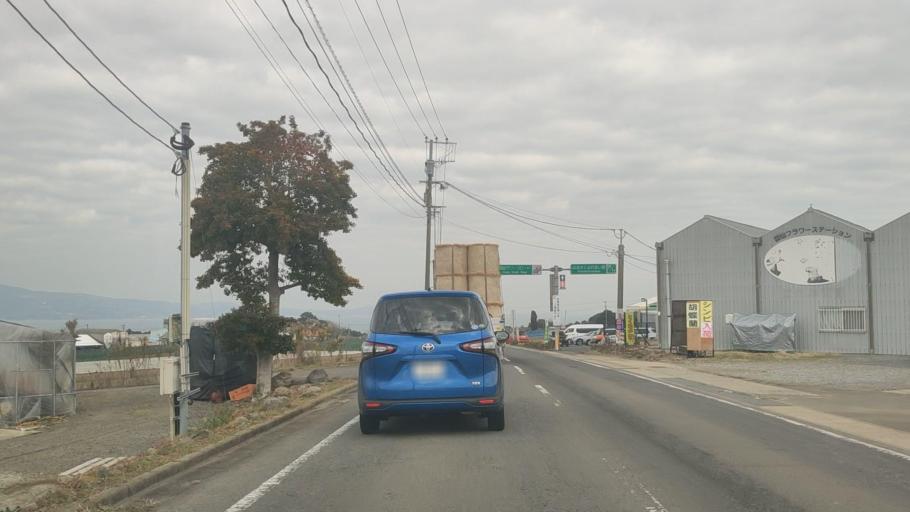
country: JP
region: Nagasaki
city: Shimabara
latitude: 32.8401
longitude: 130.2144
